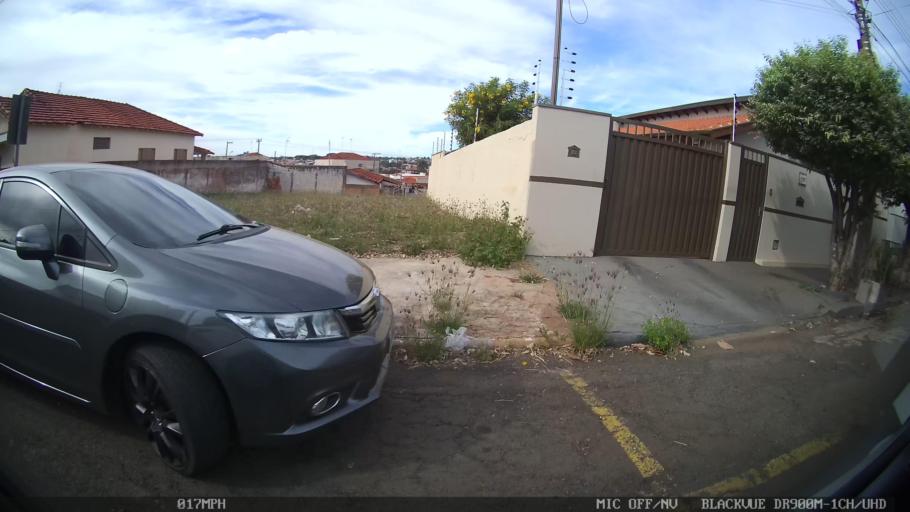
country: BR
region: Sao Paulo
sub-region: Catanduva
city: Catanduva
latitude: -21.1441
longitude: -48.9796
